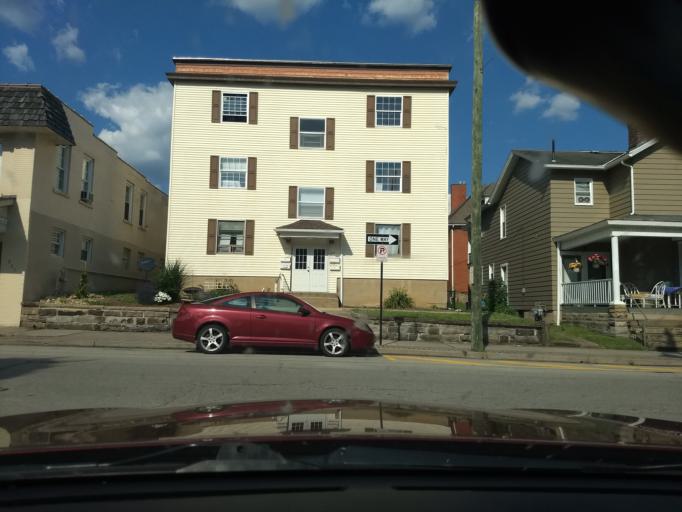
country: US
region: Pennsylvania
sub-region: Westmoreland County
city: Irwin
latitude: 40.3297
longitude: -79.7110
